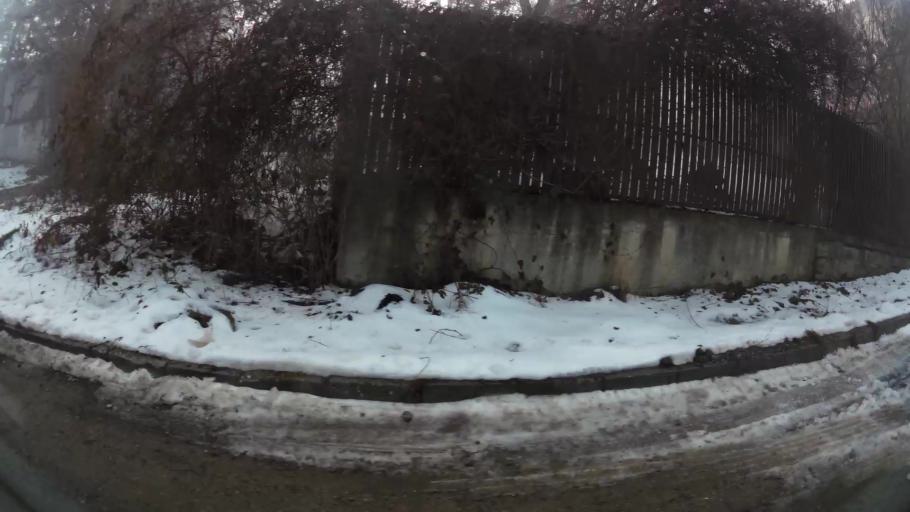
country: BG
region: Sofia-Capital
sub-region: Stolichna Obshtina
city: Sofia
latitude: 42.6578
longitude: 23.2489
